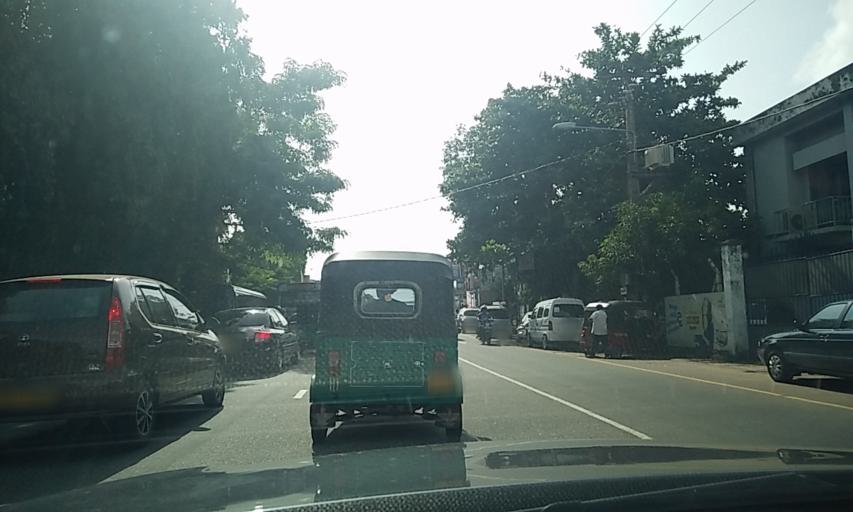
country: LK
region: Western
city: Maharagama
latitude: 6.8458
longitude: 79.9288
